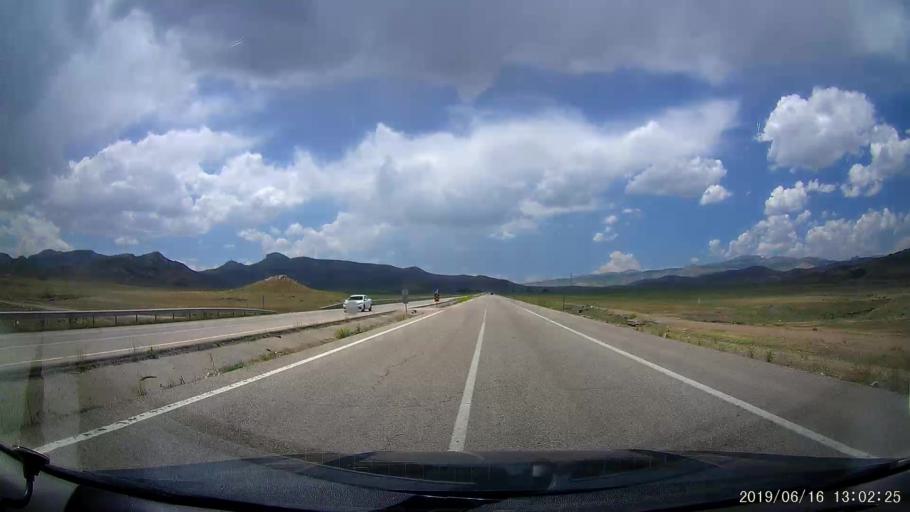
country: TR
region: Agri
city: Sulucem
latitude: 39.5746
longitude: 43.8168
